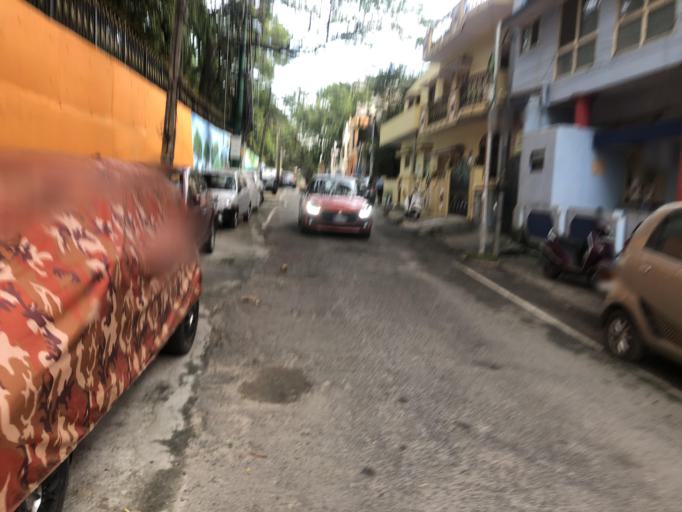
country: IN
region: Karnataka
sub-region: Bangalore Urban
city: Bangalore
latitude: 12.9402
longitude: 77.5469
